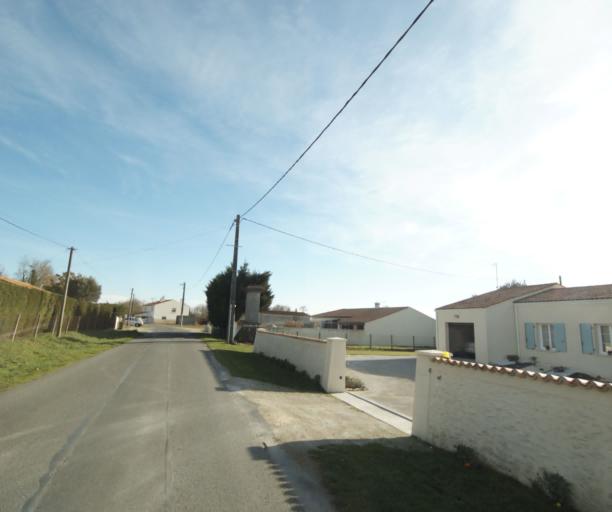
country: FR
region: Poitou-Charentes
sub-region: Departement de la Charente-Maritime
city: Chaniers
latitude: 45.7163
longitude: -0.5550
